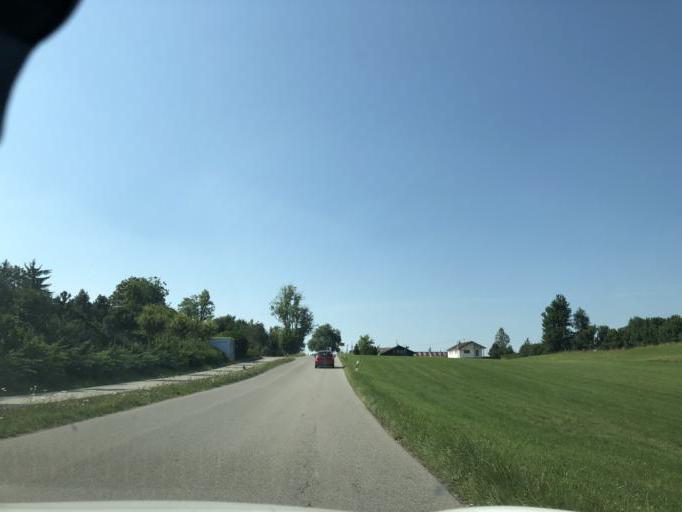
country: DE
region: Bavaria
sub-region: Swabia
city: Oy-Mittelberg
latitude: 47.6397
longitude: 10.4592
